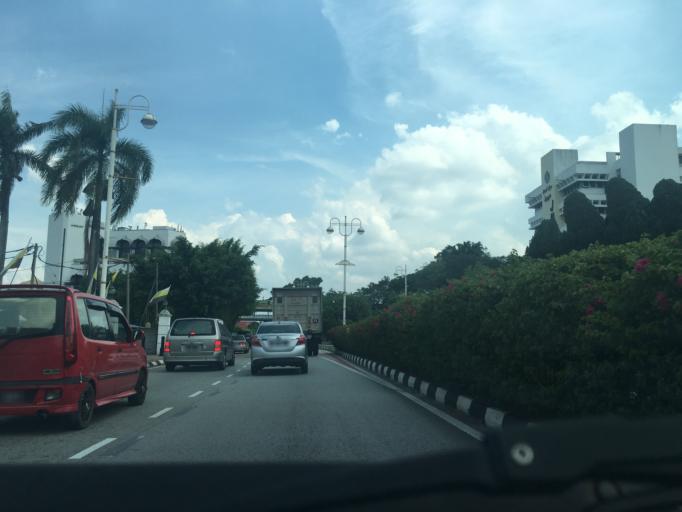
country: MY
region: Perak
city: Ipoh
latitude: 4.6050
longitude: 101.0774
